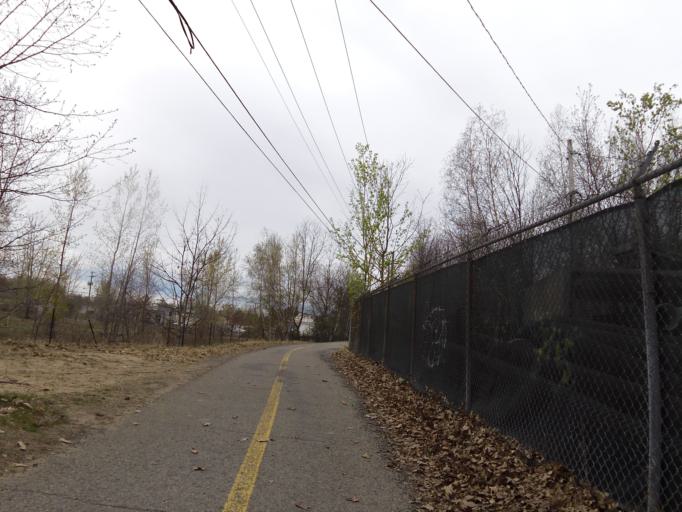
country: CA
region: Quebec
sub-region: Laurentides
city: Sainte-Marthe-sur-le-Lac
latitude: 45.5307
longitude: -73.9308
